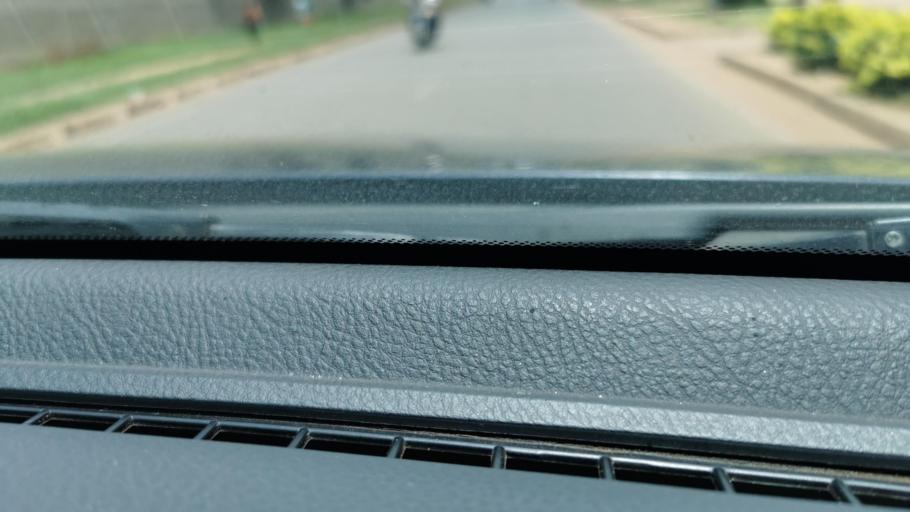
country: TG
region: Maritime
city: Lome
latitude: 6.2133
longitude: 1.1967
